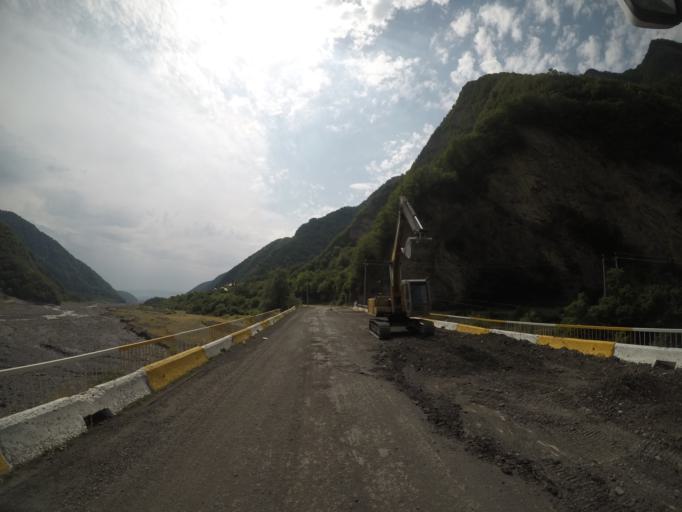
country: AZ
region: Qakh Rayon
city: Qaxbas
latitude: 41.4574
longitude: 47.0221
